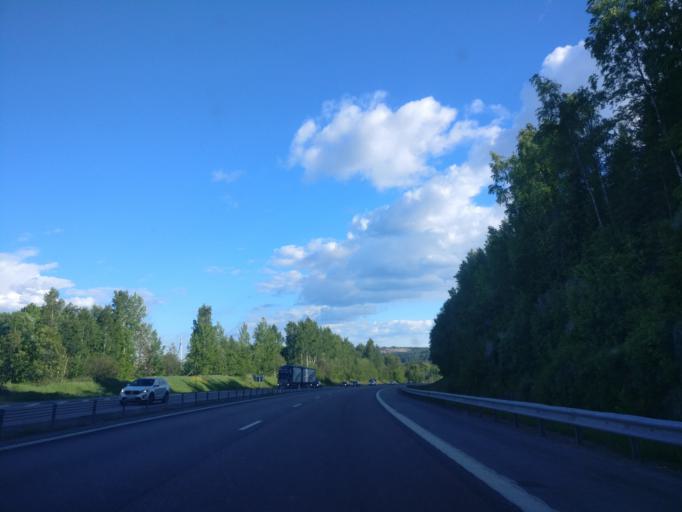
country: SE
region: Vaesternorrland
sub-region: Sundsvalls Kommun
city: Sundsbruk
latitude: 62.4564
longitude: 17.3449
